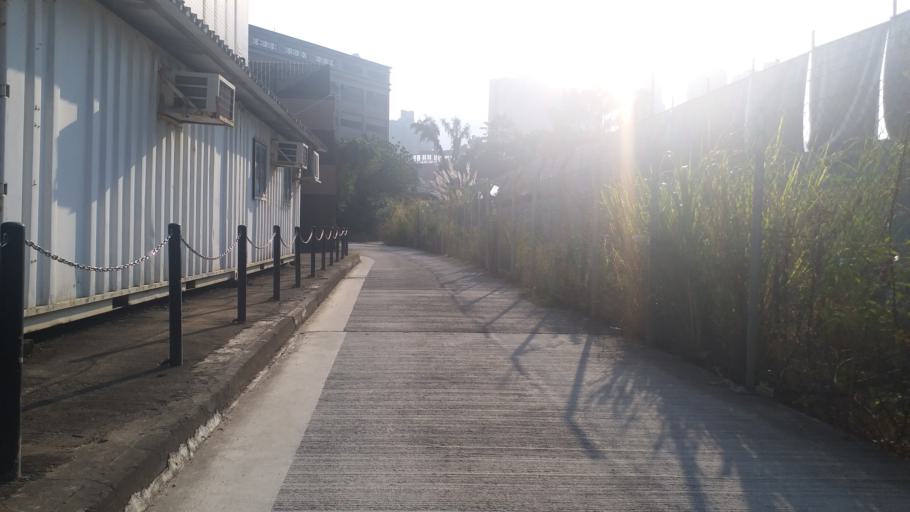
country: HK
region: Tuen Mun
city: Tuen Mun
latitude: 22.4107
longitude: 113.9730
